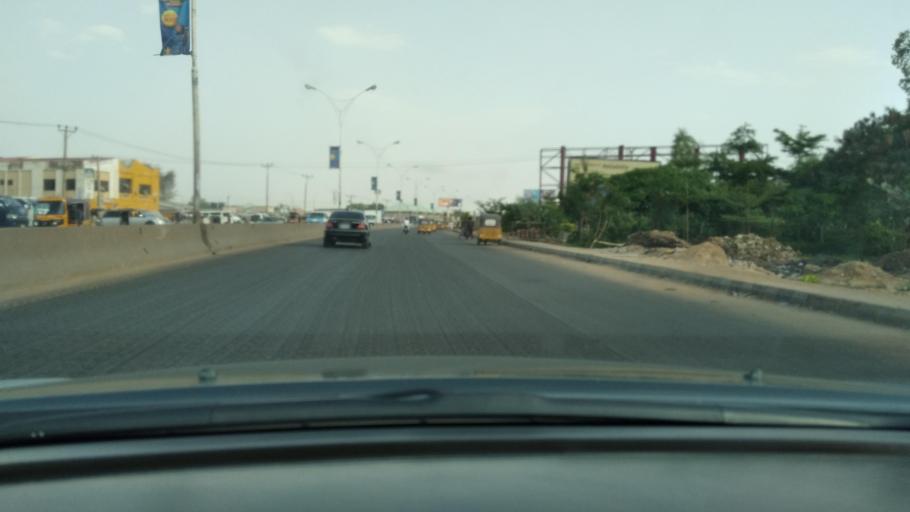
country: NG
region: Kano
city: Kano
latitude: 11.9518
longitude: 8.5647
